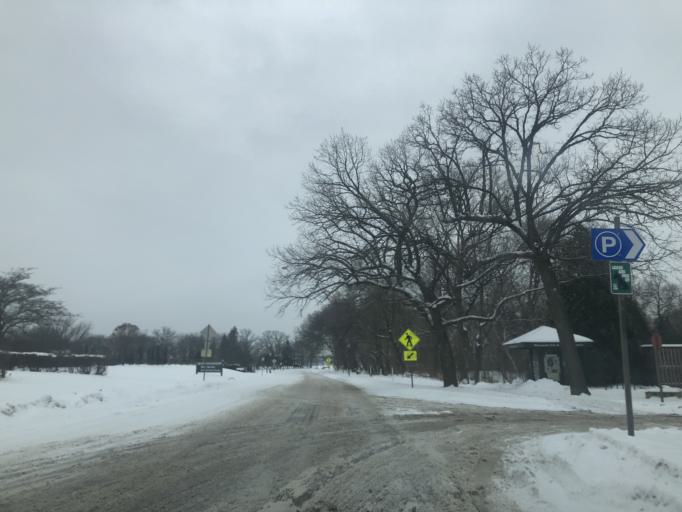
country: US
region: Minnesota
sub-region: Hennepin County
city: Richfield
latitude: 44.9280
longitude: -93.2960
